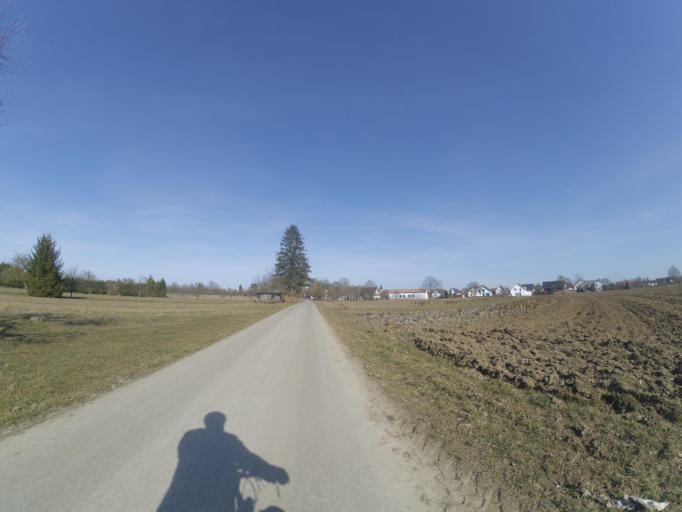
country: DE
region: Baden-Wuerttemberg
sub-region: Regierungsbezirk Stuttgart
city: Sontheim an der Brenz
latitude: 48.5484
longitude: 10.2850
